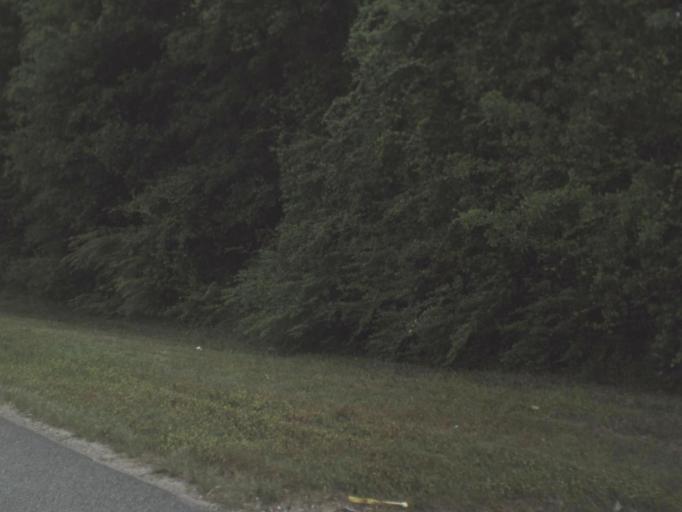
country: US
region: Florida
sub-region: Escambia County
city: Ensley
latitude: 30.5435
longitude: -87.2817
